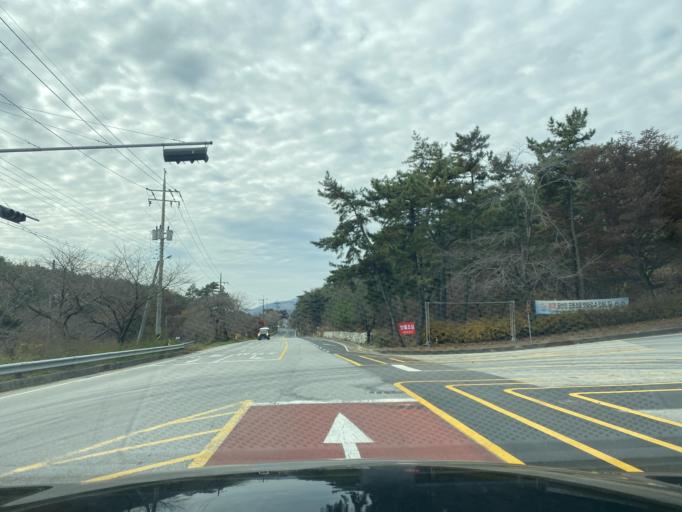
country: KR
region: Chungcheongnam-do
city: Hongsung
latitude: 36.6568
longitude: 126.6248
